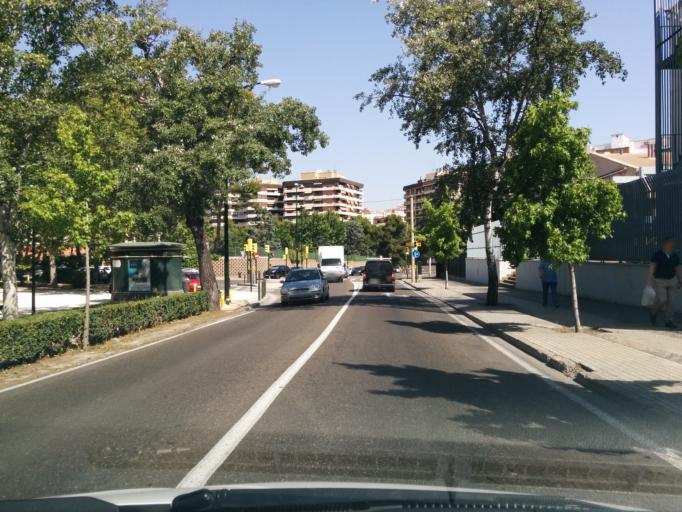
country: ES
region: Aragon
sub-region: Provincia de Zaragoza
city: Delicias
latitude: 41.6363
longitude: -0.8940
